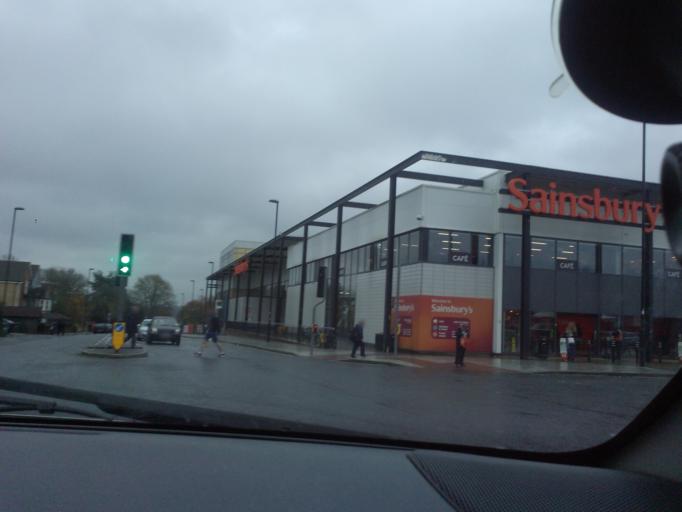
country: GB
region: England
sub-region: Southampton
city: Southampton
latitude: 50.9269
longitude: -1.3909
